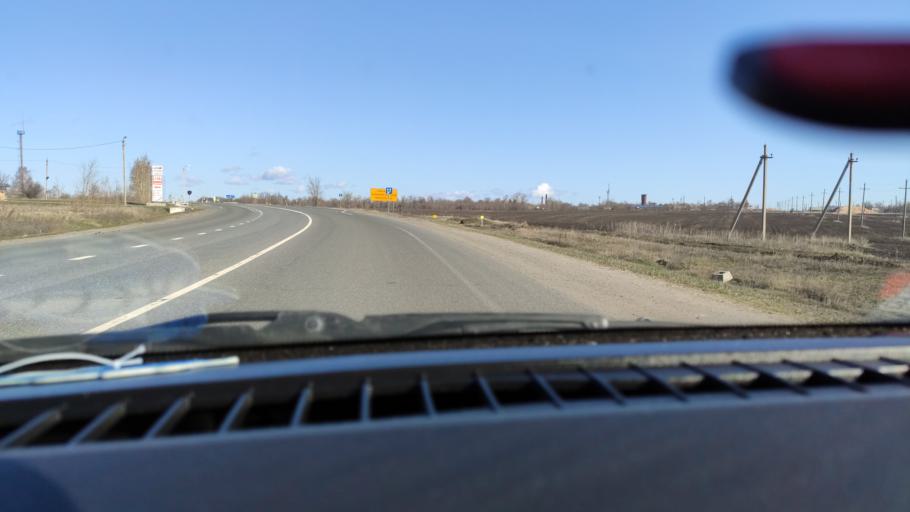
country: RU
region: Samara
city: Syzran'
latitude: 53.2057
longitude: 48.5094
